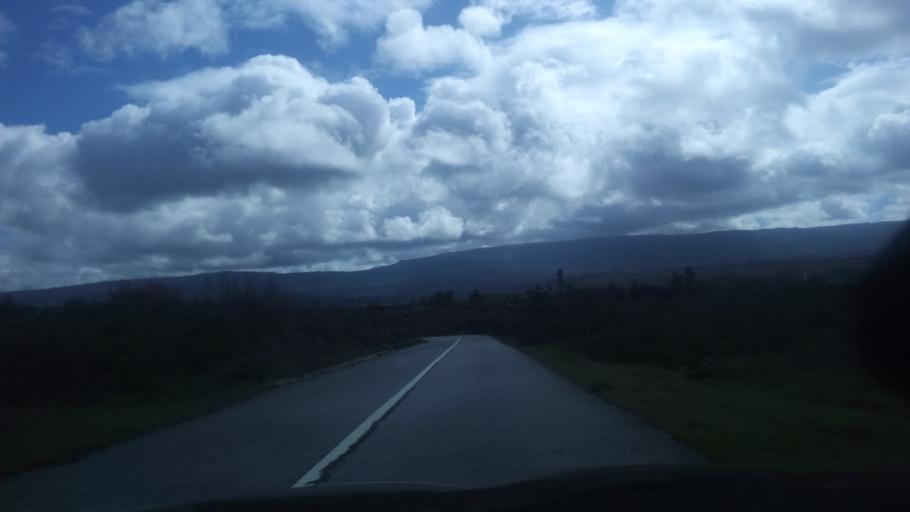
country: PT
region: Guarda
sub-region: Fornos de Algodres
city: Fornos de Algodres
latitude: 40.5972
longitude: -7.5082
